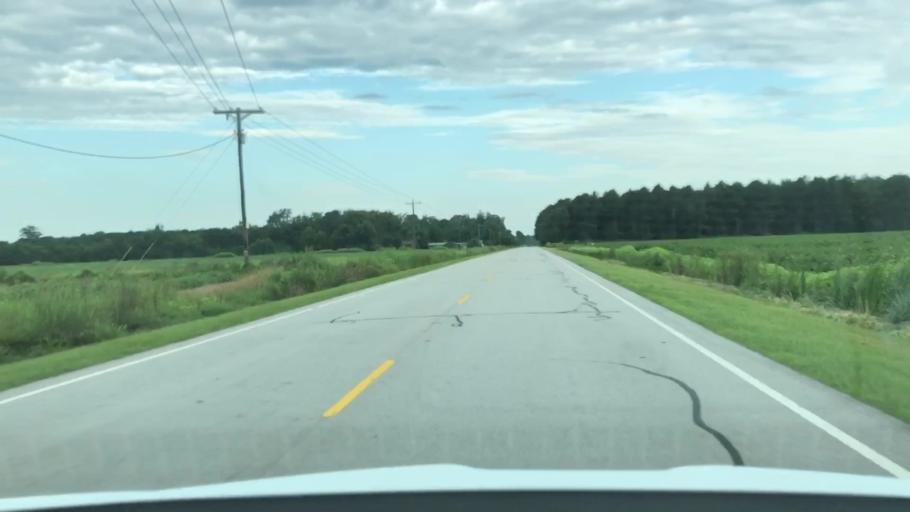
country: US
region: North Carolina
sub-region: Jones County
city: Trenton
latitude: 35.0813
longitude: -77.4353
